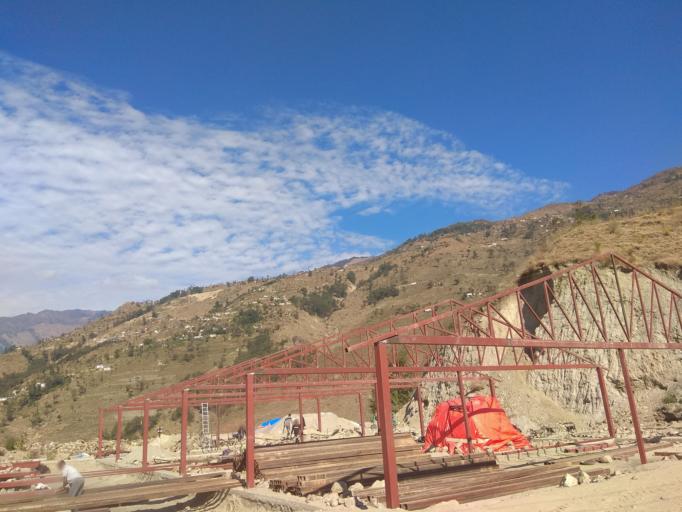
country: NP
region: Far Western
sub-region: Seti Zone
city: Achham
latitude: 29.2478
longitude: 81.6287
